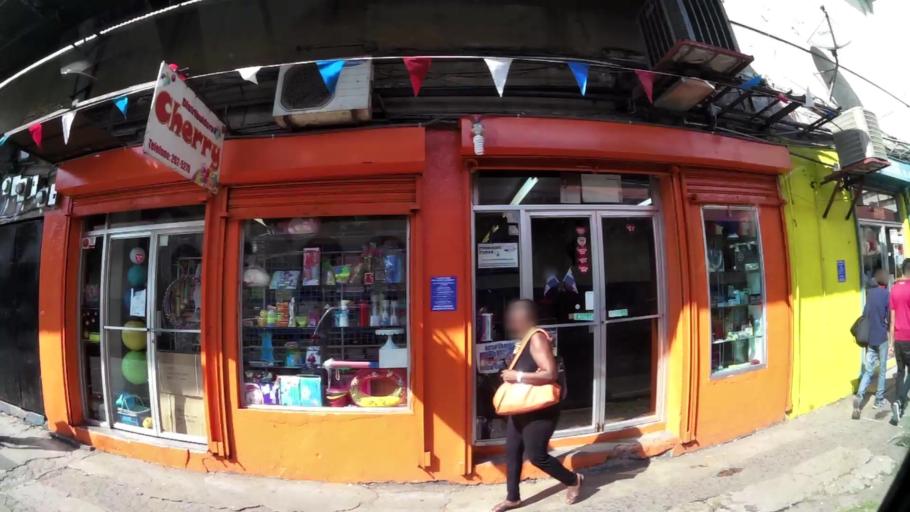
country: PA
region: Panama
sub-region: Distrito de Panama
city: Ancon
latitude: 8.9575
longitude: -79.5391
